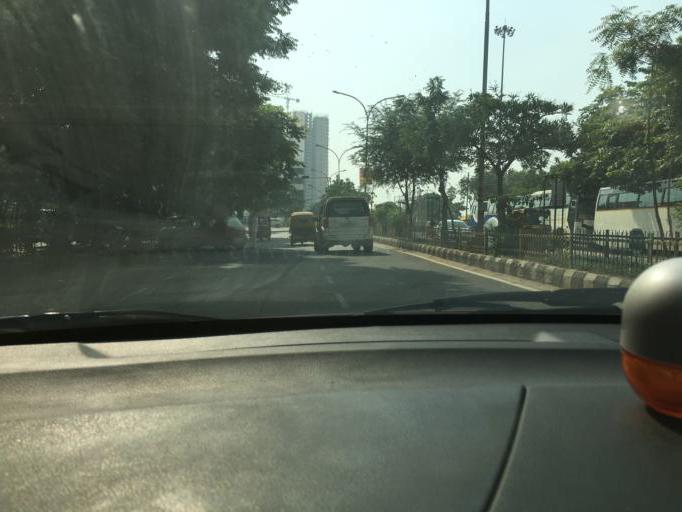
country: IN
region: Uttar Pradesh
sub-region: Gautam Buddha Nagar
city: Noida
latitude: 28.5830
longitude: 77.3526
